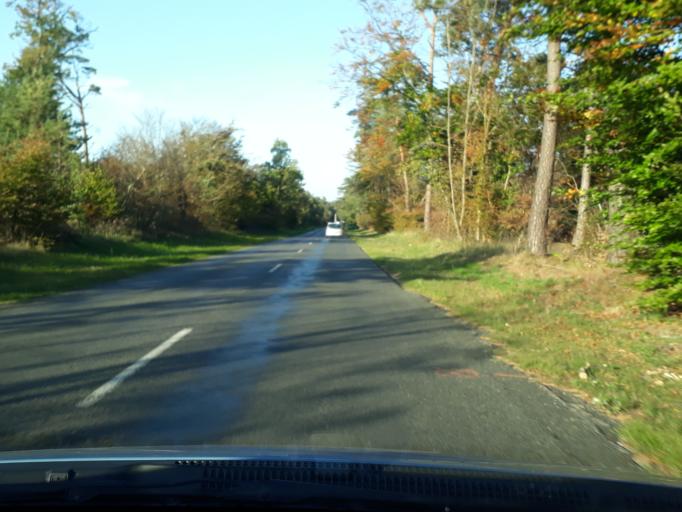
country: FR
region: Ile-de-France
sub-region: Departement de Seine-et-Marne
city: Avon
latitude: 48.4380
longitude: 2.7155
